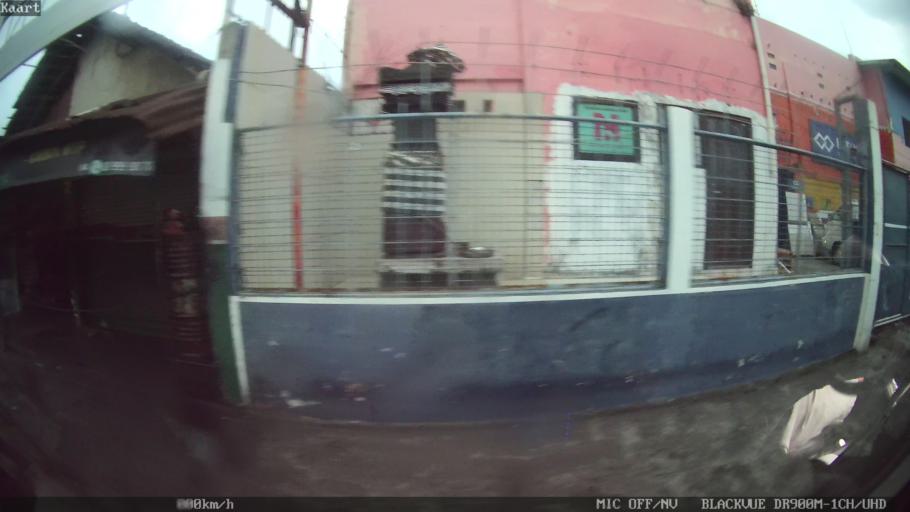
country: ID
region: Bali
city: Banjar Kayangan
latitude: -8.6342
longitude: 115.2233
